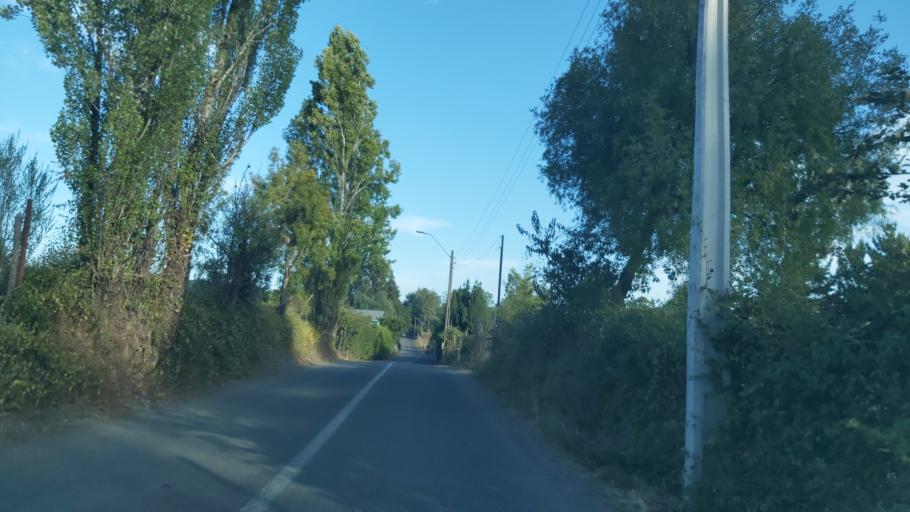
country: CL
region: Biobio
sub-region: Provincia de Biobio
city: La Laja
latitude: -37.1611
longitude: -72.9169
